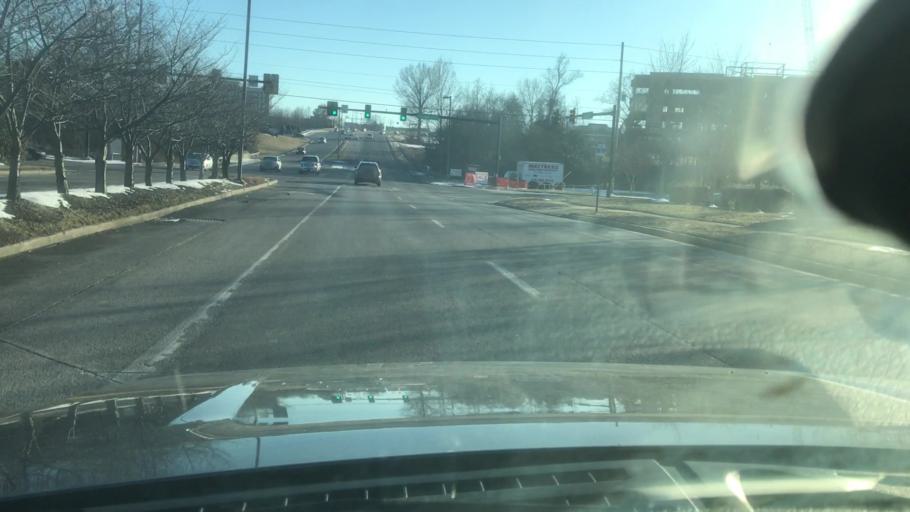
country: US
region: Tennessee
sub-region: Williamson County
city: Franklin
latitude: 35.9423
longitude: -86.8211
